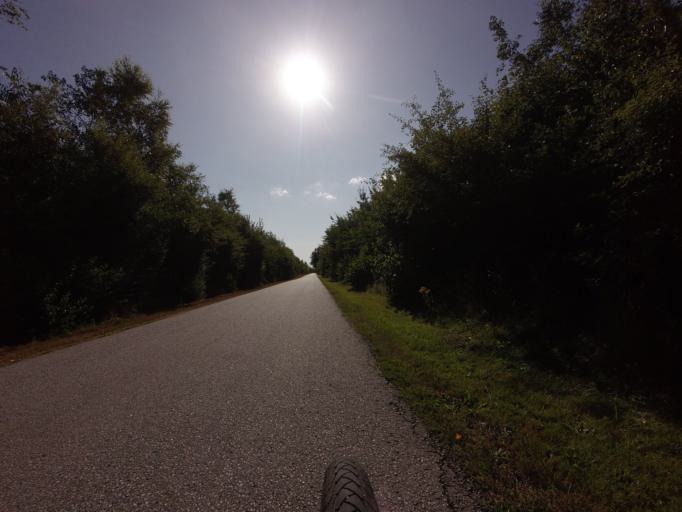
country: DK
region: North Denmark
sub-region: Hjorring Kommune
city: Vra
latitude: 57.3978
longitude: 9.9776
